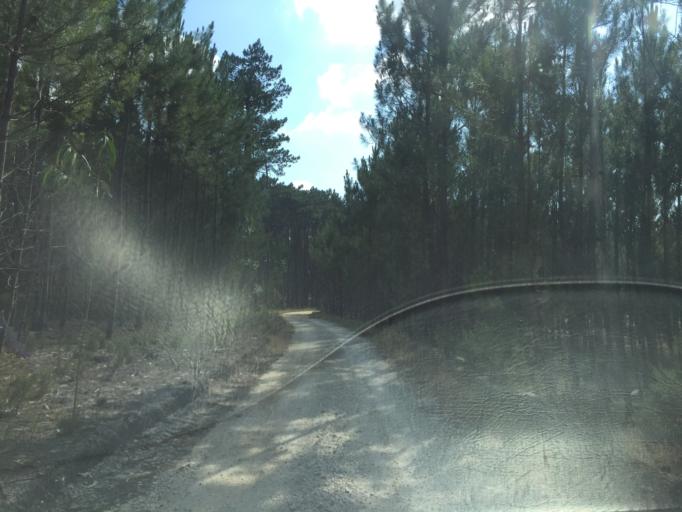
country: PT
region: Leiria
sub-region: Leiria
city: Monte Redondo
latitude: 39.9622
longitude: -8.8084
